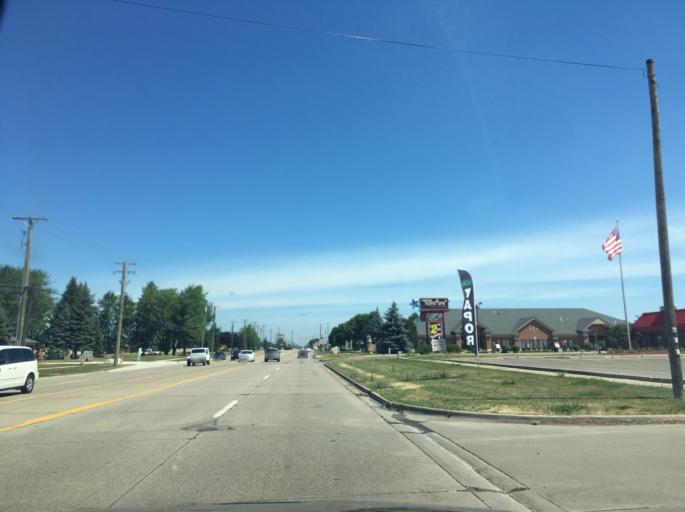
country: US
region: Michigan
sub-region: Macomb County
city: Clinton
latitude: 42.6067
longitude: -82.9723
